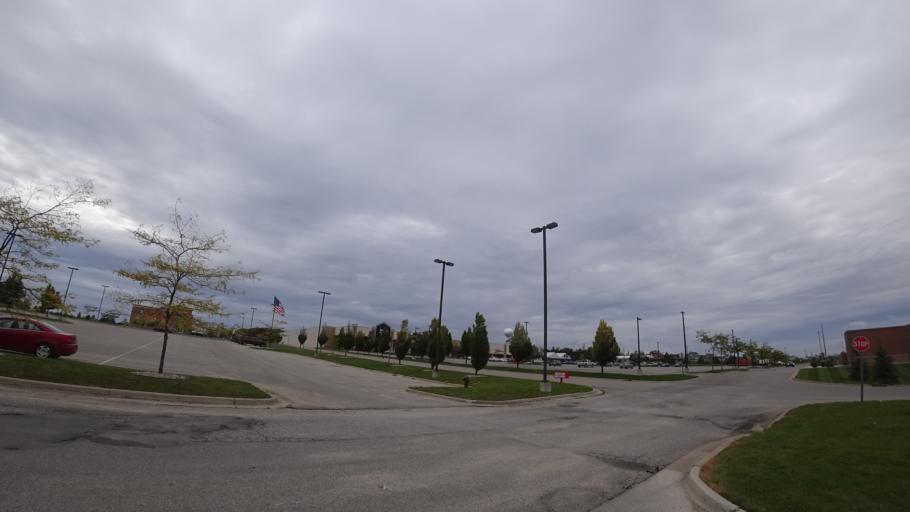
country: US
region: Michigan
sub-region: Emmet County
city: Petoskey
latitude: 45.3462
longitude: -84.9719
